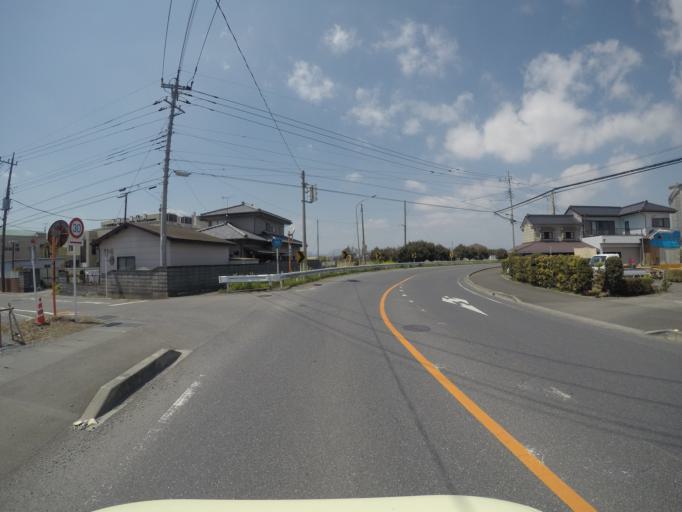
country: JP
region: Tochigi
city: Mibu
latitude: 36.4318
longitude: 139.7945
